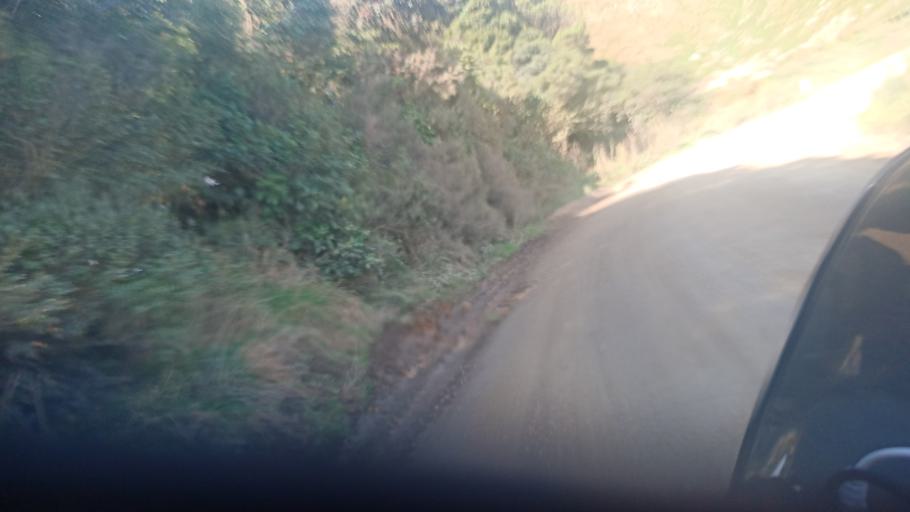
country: NZ
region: Gisborne
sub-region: Gisborne District
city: Gisborne
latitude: -38.4334
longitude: 177.5552
